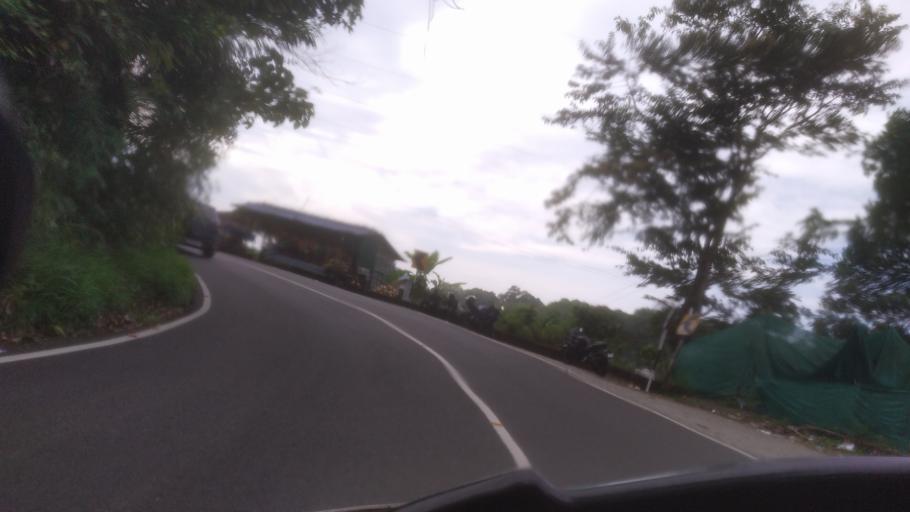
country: IN
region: Kerala
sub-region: Idukki
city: Kuttampuzha
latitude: 10.0586
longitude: 76.8018
